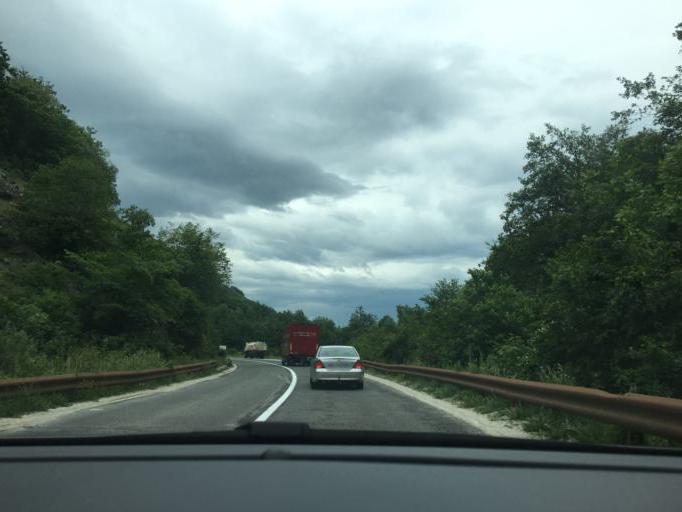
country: MK
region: Drugovo
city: Drugovo
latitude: 41.4765
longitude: 20.8674
